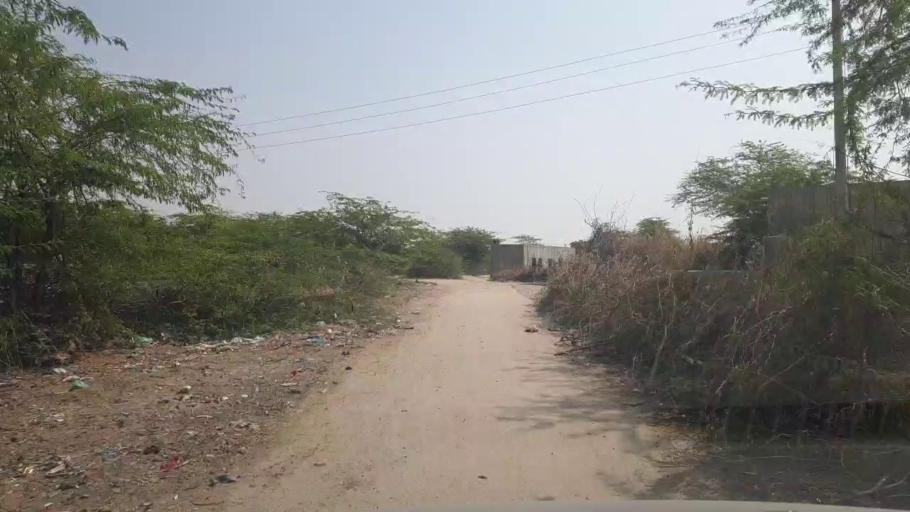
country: PK
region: Sindh
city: Chor
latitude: 25.4868
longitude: 69.7842
